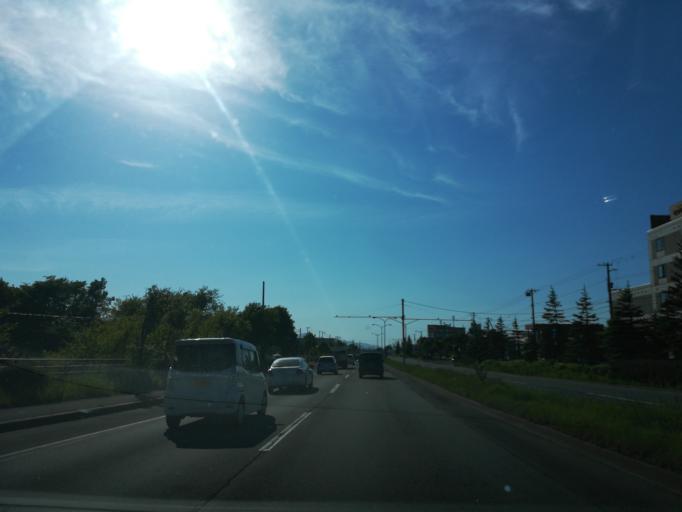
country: JP
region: Hokkaido
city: Kitahiroshima
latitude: 43.0127
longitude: 141.5062
